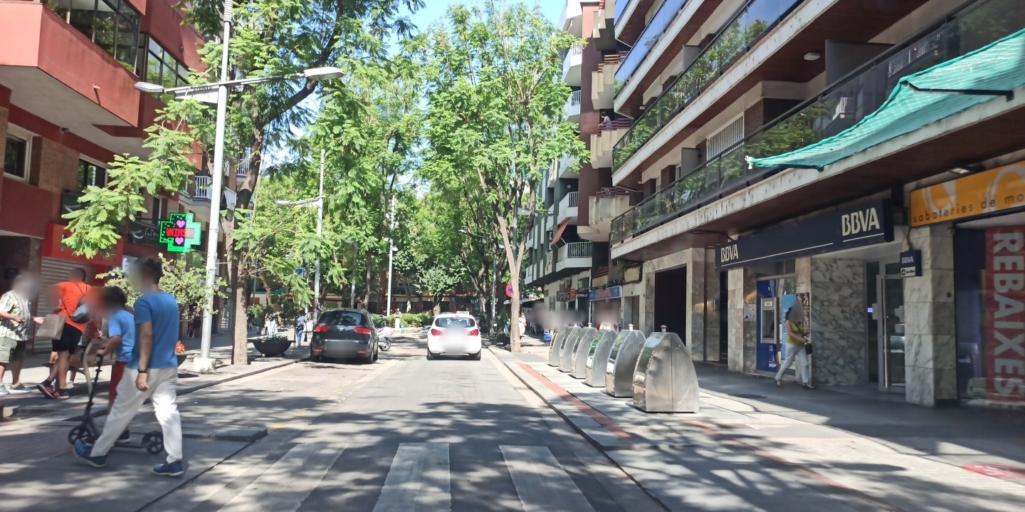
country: ES
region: Catalonia
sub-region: Provincia de Barcelona
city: Cerdanyola del Valles
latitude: 41.4932
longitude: 2.1443
